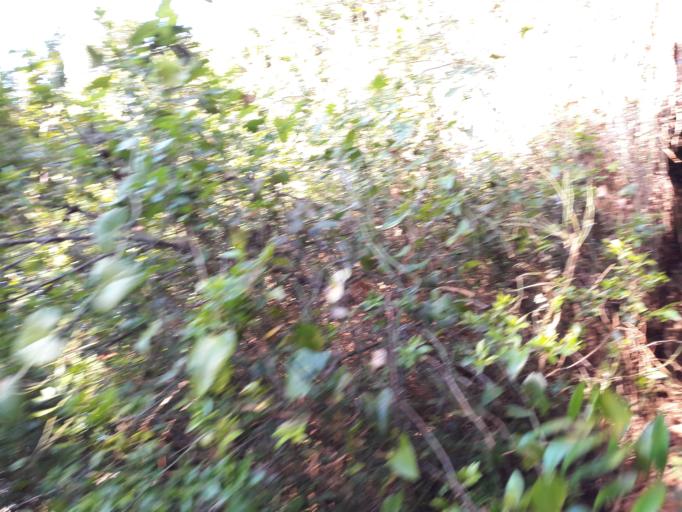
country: HR
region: Dubrovacko-Neretvanska
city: Orebic
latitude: 43.0232
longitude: 17.1585
